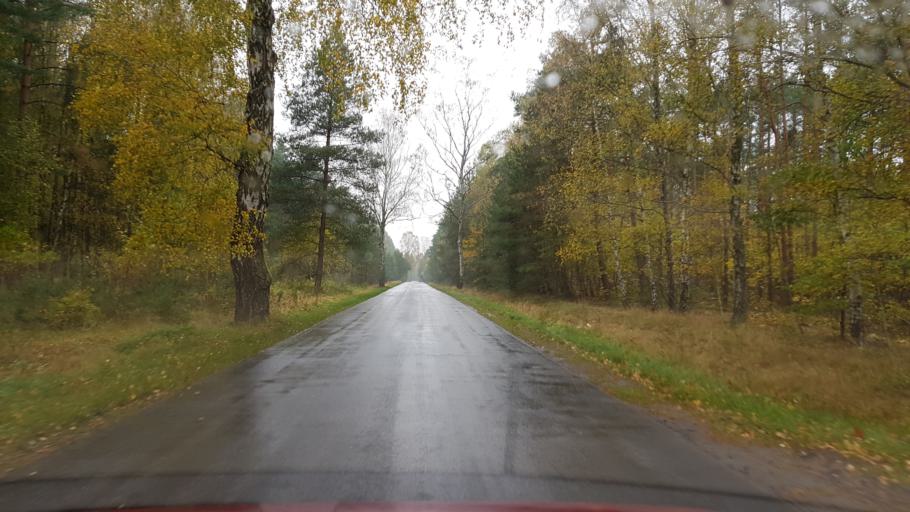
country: PL
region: West Pomeranian Voivodeship
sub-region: Powiat walecki
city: Walcz
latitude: 53.3537
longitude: 16.5548
